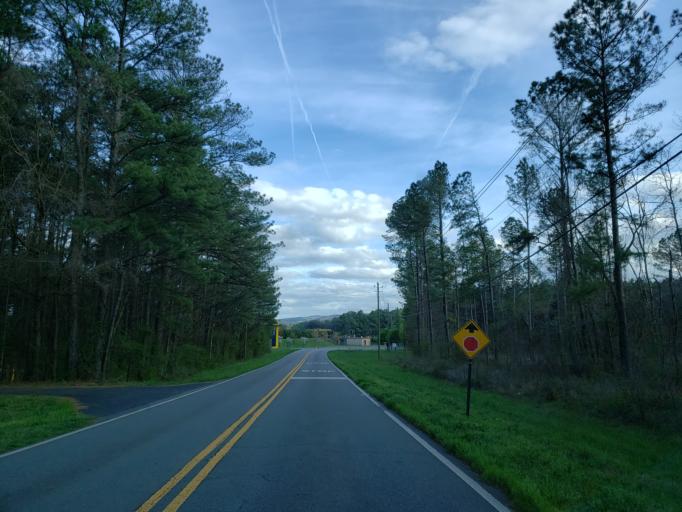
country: US
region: Georgia
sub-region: Bartow County
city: Cartersville
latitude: 34.2387
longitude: -84.8069
